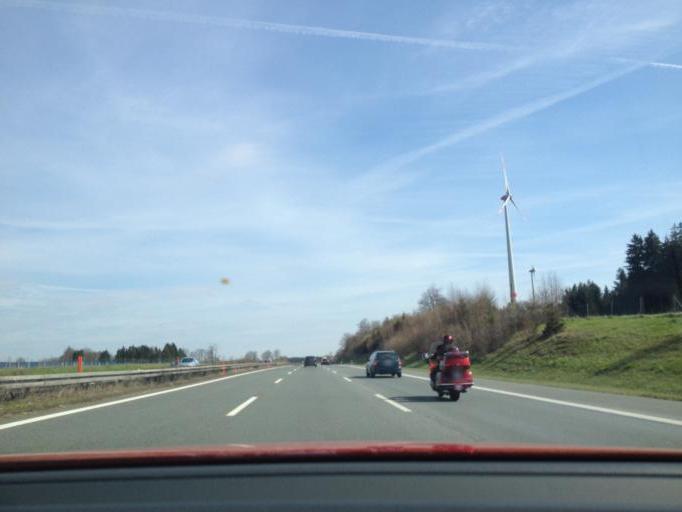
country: DE
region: Bavaria
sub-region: Upper Franconia
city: Gefrees
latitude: 50.1441
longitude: 11.7441
